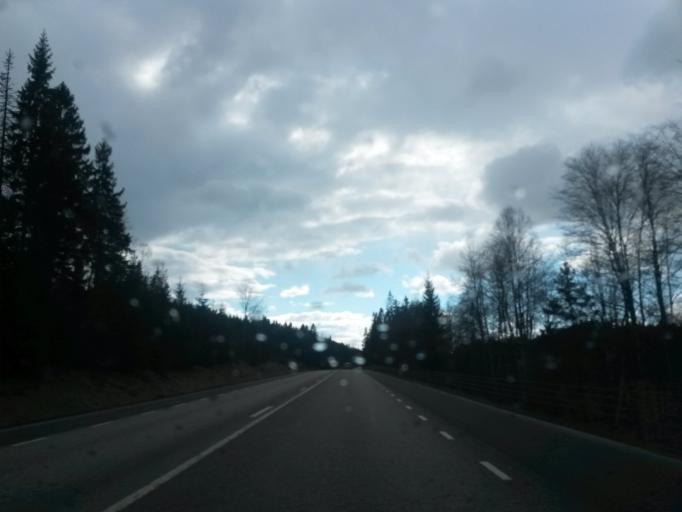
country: SE
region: Vaestra Goetaland
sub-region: Skovde Kommun
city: Skultorp
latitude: 58.3911
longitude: 13.7562
